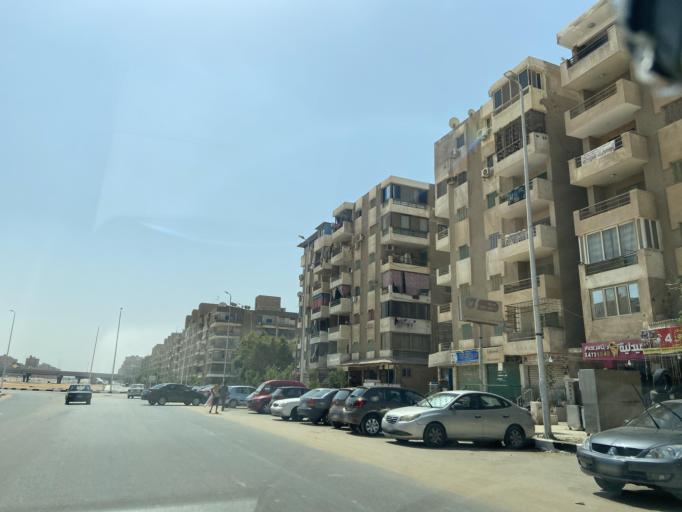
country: EG
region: Muhafazat al Qahirah
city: Cairo
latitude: 30.0614
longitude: 31.3780
